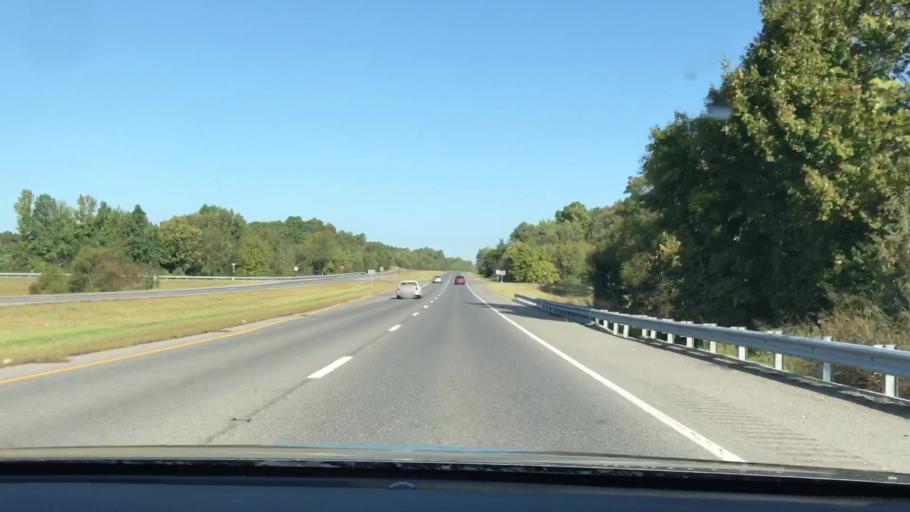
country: US
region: Kentucky
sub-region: Marshall County
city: Benton
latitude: 36.7739
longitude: -88.3179
